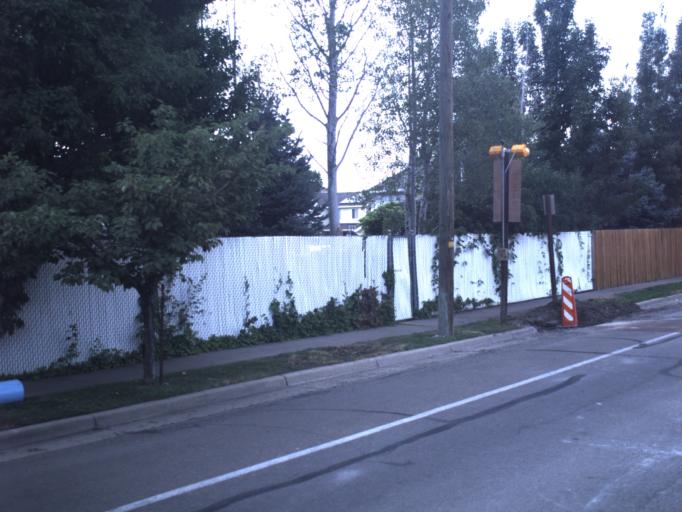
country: US
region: Utah
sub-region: Davis County
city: Centerville
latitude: 40.9099
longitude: -111.8790
